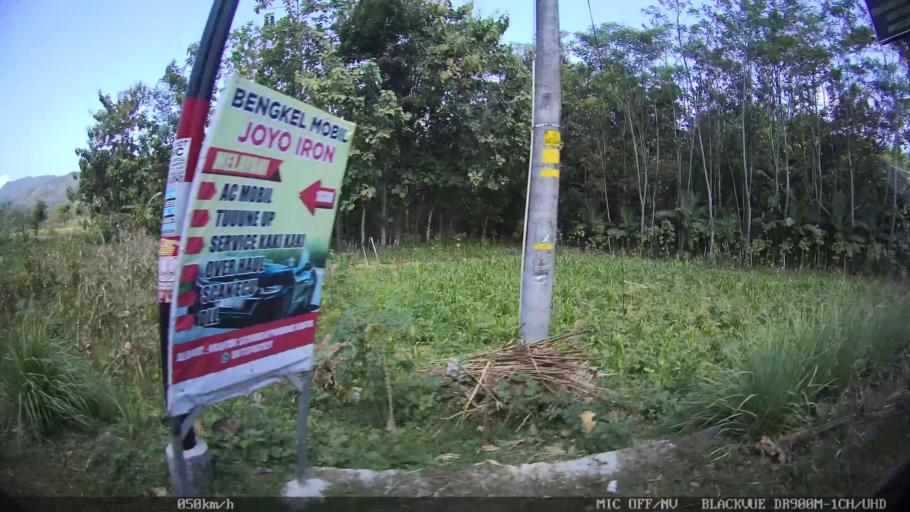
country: ID
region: Daerah Istimewa Yogyakarta
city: Pundong
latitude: -7.9831
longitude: 110.3351
